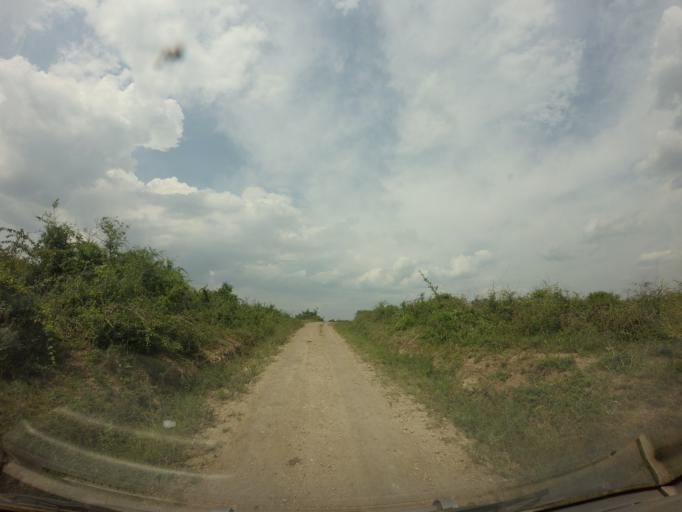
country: UG
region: Western Region
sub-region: Rubirizi District
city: Rubirizi
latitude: -0.2101
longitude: 29.9157
